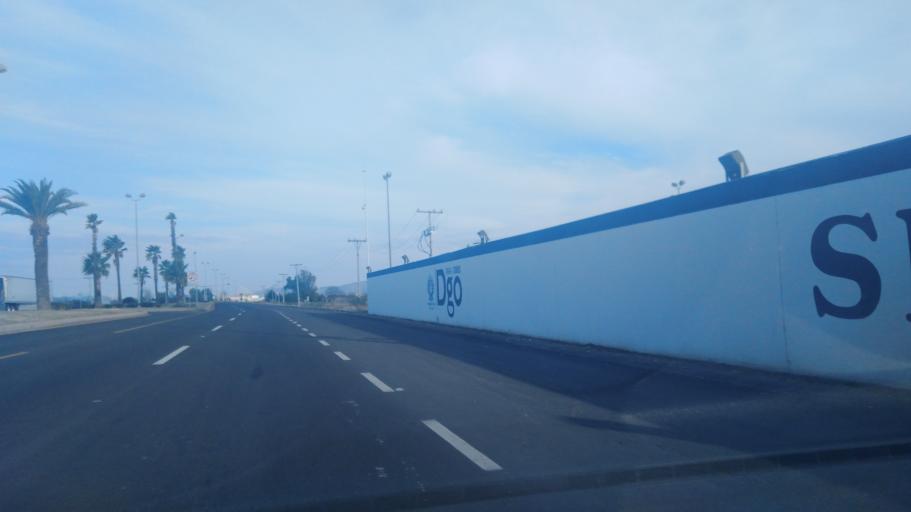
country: MX
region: Durango
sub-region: Durango
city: Jose Refugio Salcido
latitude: 24.0220
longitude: -104.5342
